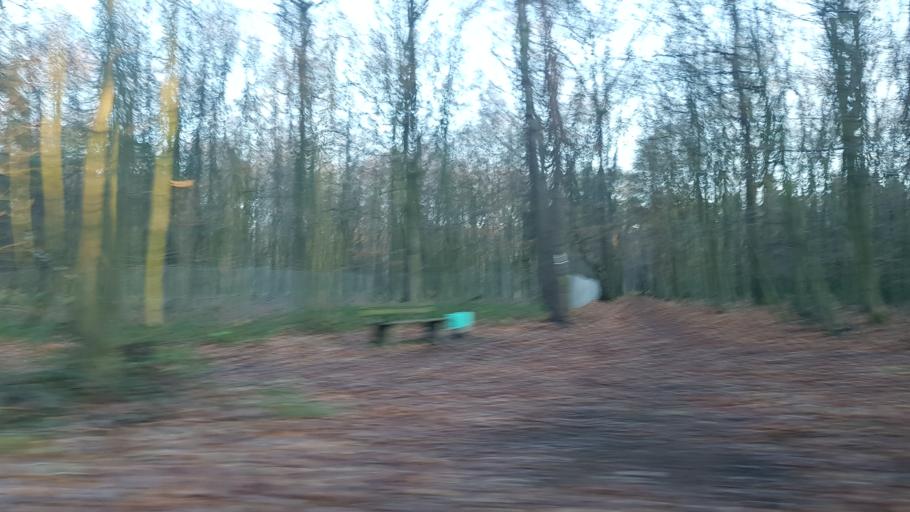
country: DE
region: North Rhine-Westphalia
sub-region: Regierungsbezirk Dusseldorf
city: Duisburg
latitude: 51.4070
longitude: 6.8203
